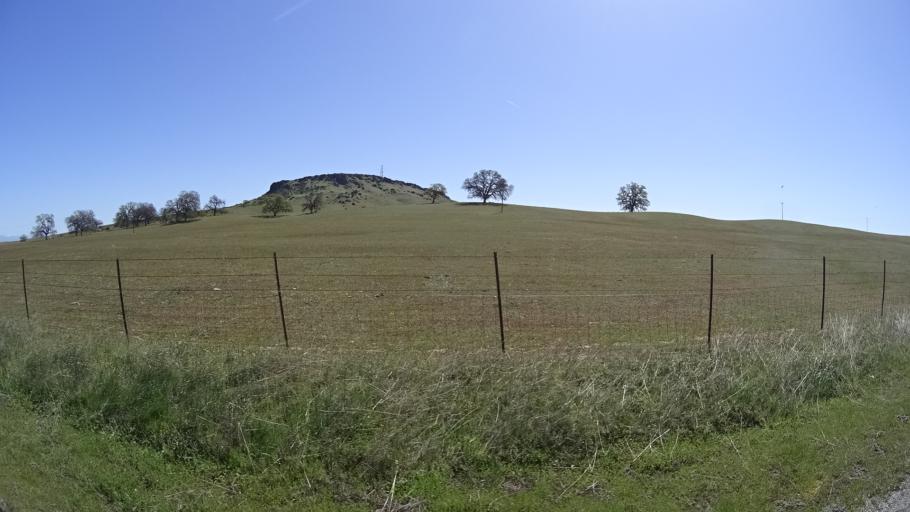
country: US
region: California
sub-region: Glenn County
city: Orland
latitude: 39.7596
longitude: -122.3447
